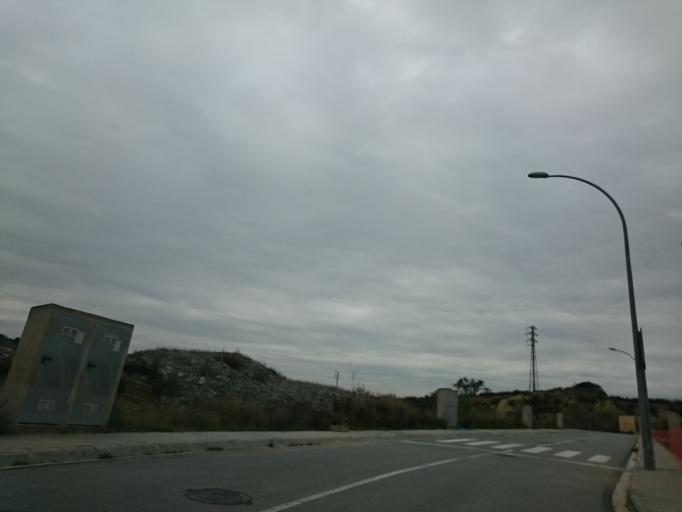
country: ES
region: Catalonia
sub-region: Provincia de Barcelona
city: Sant Sadurni d'Anoia
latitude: 41.4260
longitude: 1.8035
